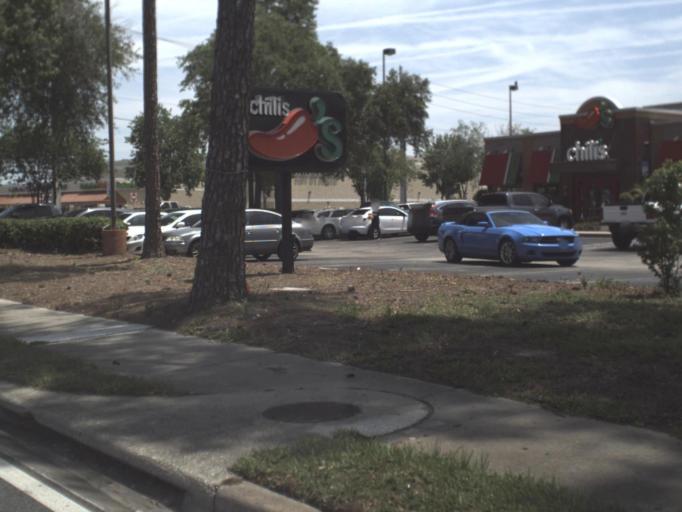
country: US
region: Florida
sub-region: Saint Johns County
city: Fruit Cove
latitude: 30.1747
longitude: -81.6279
